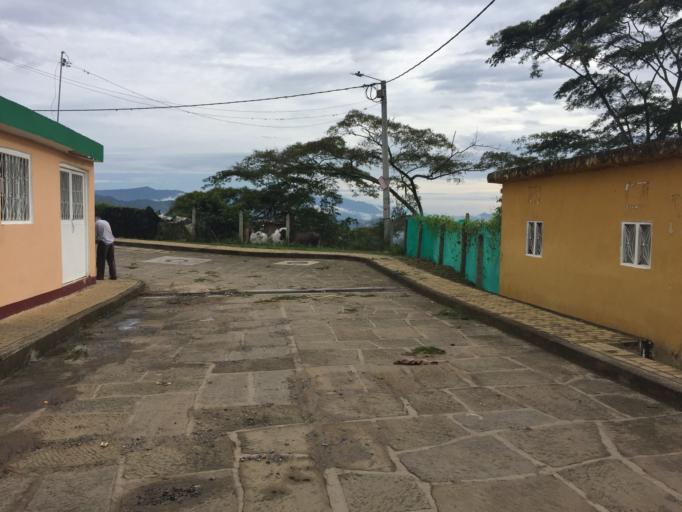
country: CO
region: Santander
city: Guepsa
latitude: 6.0175
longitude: -73.5464
